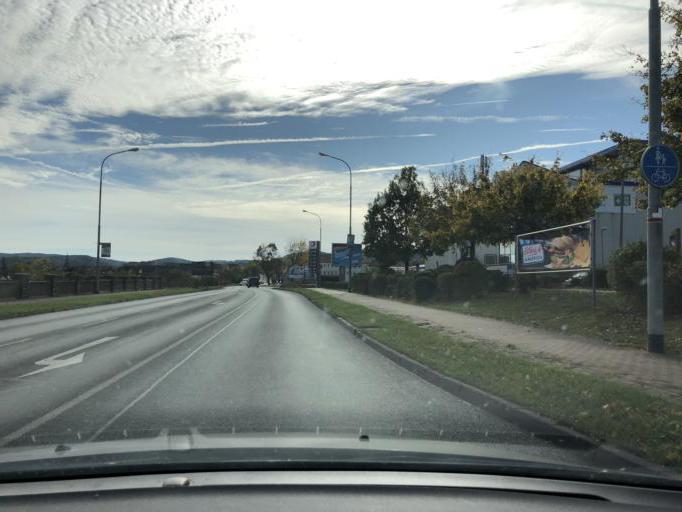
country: DE
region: Thuringia
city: Saalfeld
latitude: 50.6583
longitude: 11.3484
